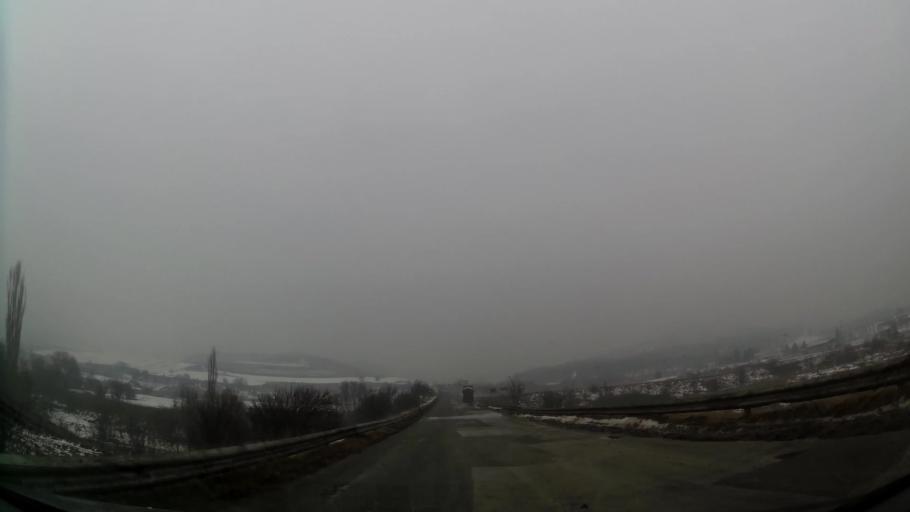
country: MK
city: Miladinovci
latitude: 41.9986
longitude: 21.6595
